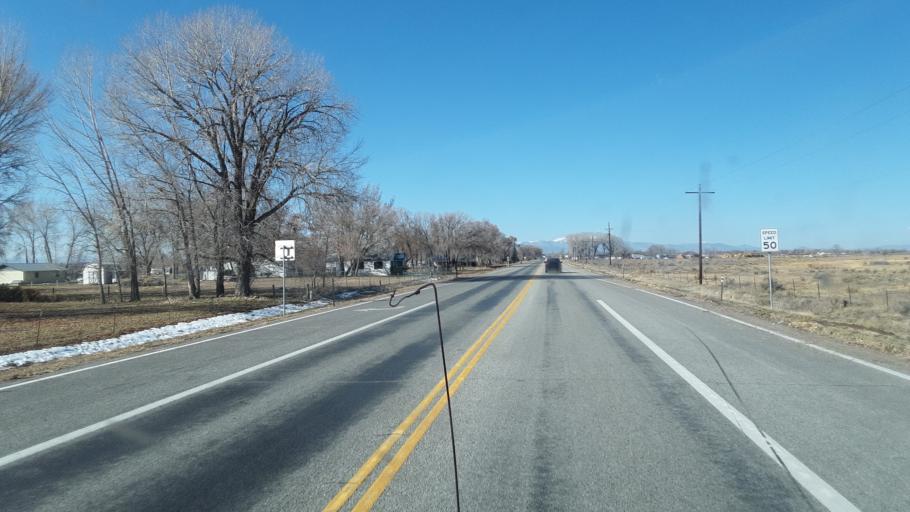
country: US
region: Colorado
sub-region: Alamosa County
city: Alamosa East
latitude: 37.4735
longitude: -105.8212
